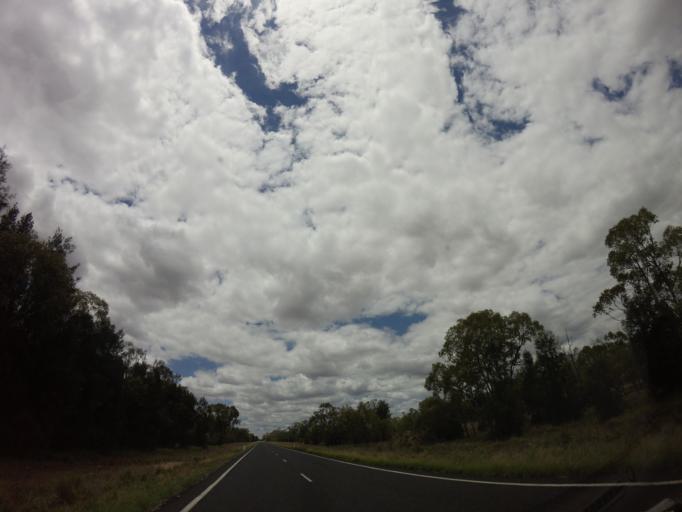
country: AU
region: Queensland
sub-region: Goondiwindi
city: Goondiwindi
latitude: -28.1672
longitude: 150.5982
